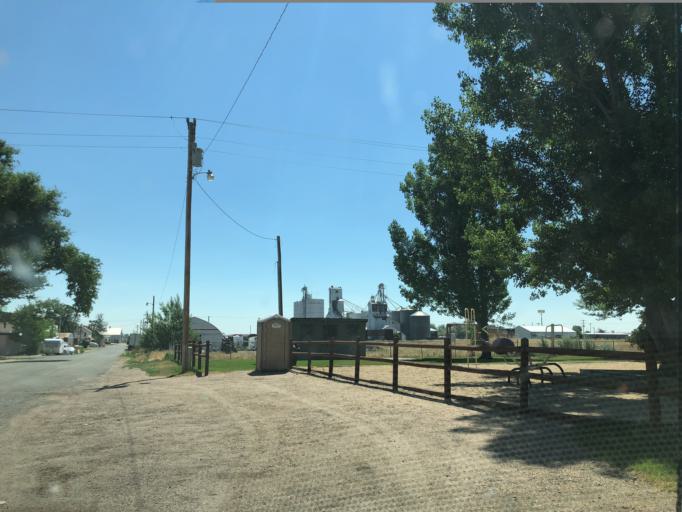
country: US
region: Colorado
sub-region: Adams County
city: Strasburg
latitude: 39.7369
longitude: -104.3247
